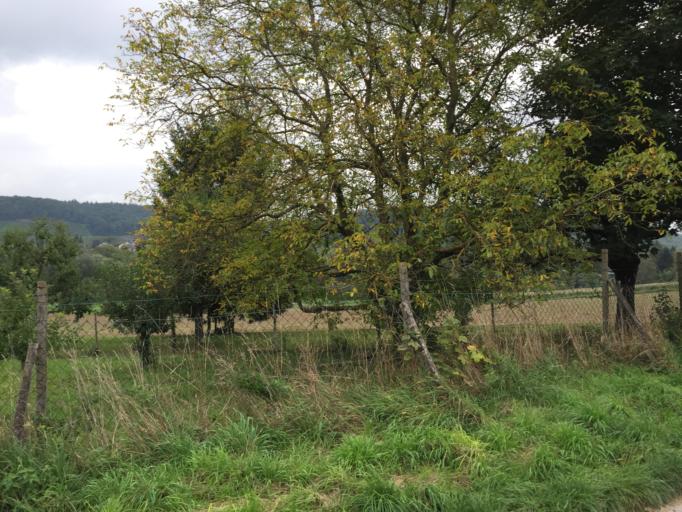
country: DE
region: Baden-Wuerttemberg
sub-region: Regierungsbezirk Stuttgart
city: Heilbronn
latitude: 49.1322
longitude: 9.2487
